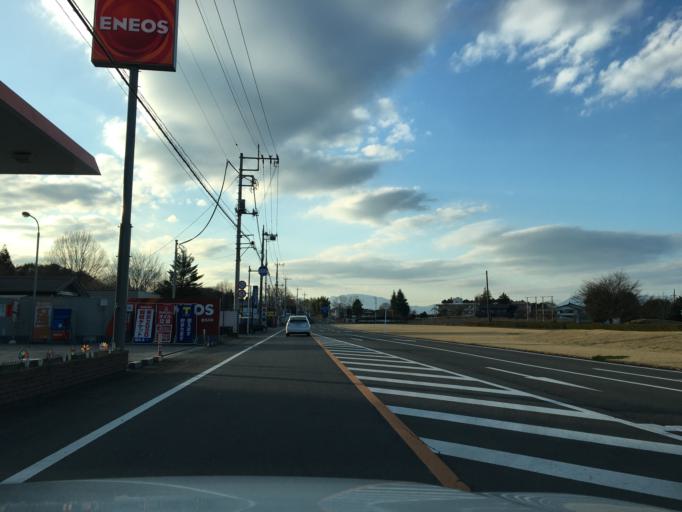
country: JP
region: Tochigi
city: Otawara
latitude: 36.8618
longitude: 140.0868
